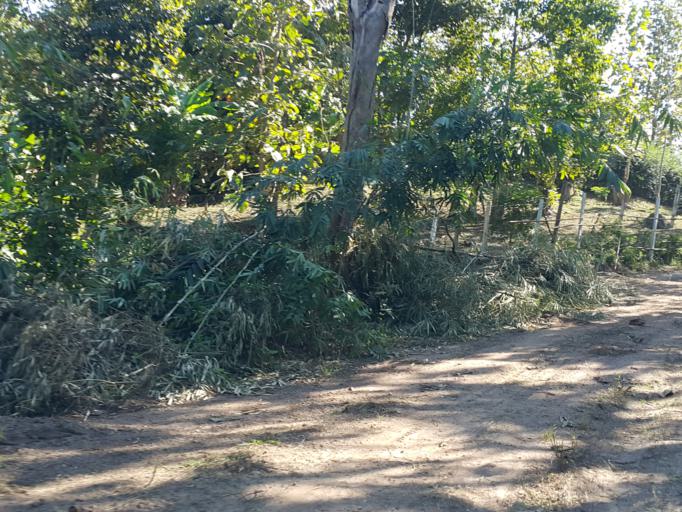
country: TH
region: Chiang Mai
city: Mae Taeng
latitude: 18.9559
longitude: 98.9008
